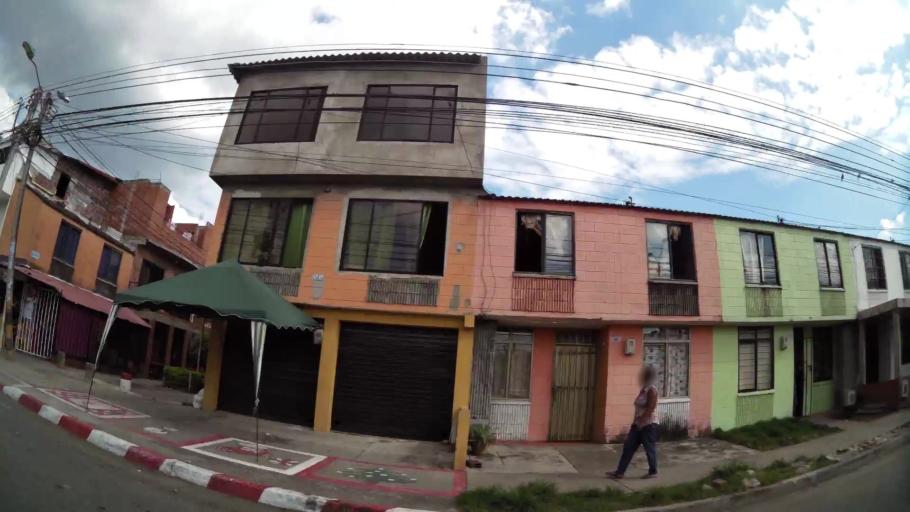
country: CO
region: Valle del Cauca
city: Cali
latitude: 3.3995
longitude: -76.5043
